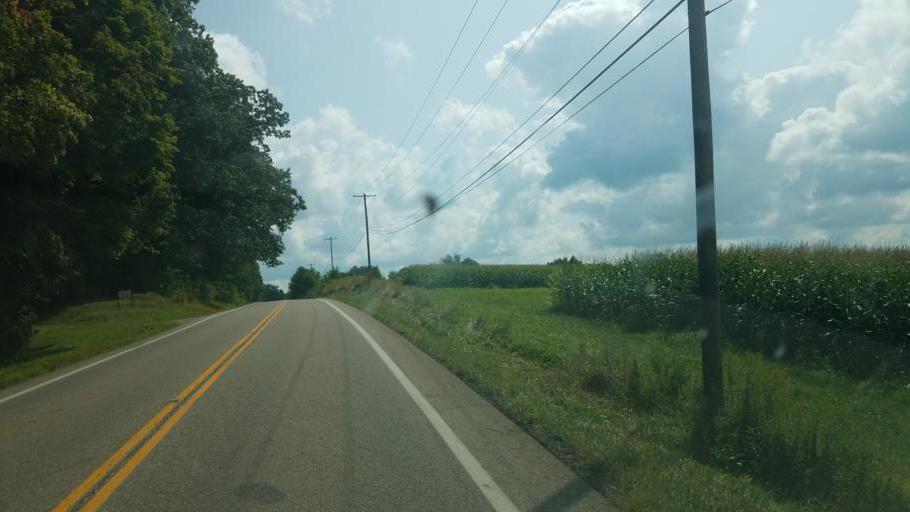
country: US
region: Ohio
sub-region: Columbiana County
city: Lisbon
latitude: 40.7843
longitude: -80.8342
